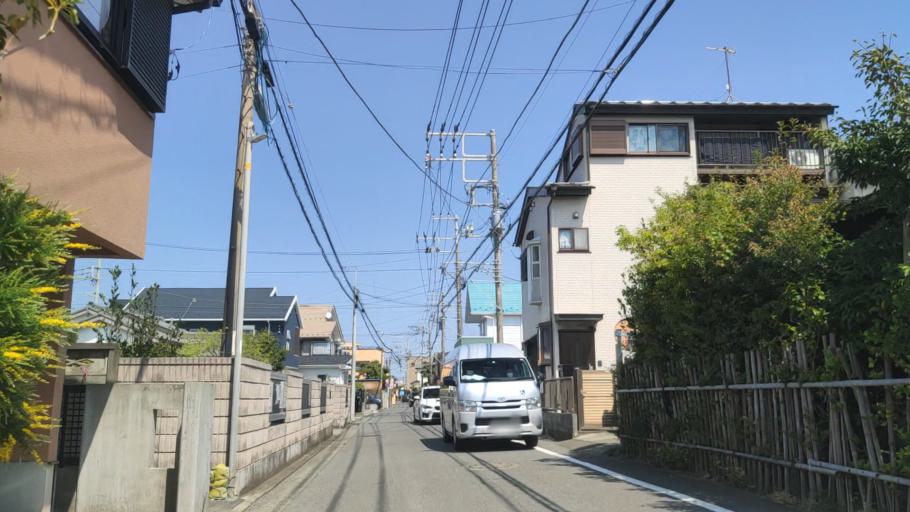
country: JP
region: Kanagawa
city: Oiso
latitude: 35.3135
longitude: 139.3214
